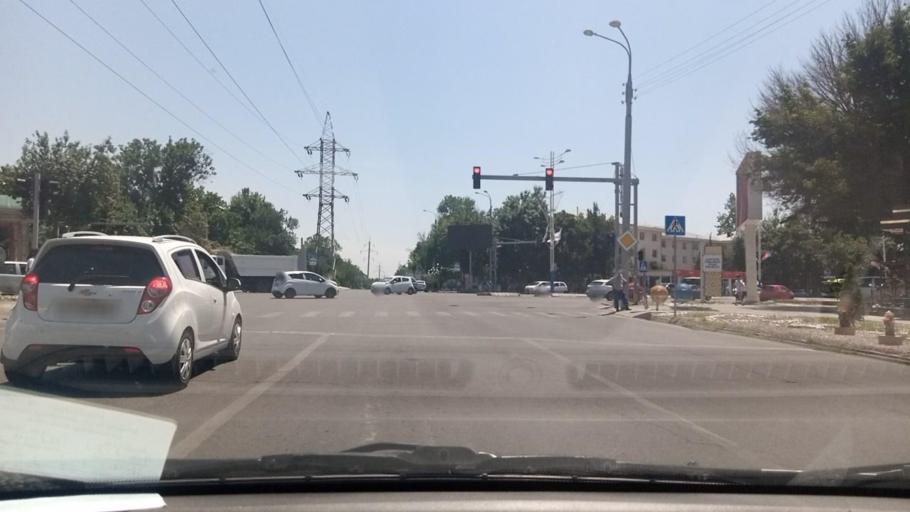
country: UZ
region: Toshkent Shahri
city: Tashkent
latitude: 41.2926
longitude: 69.1940
